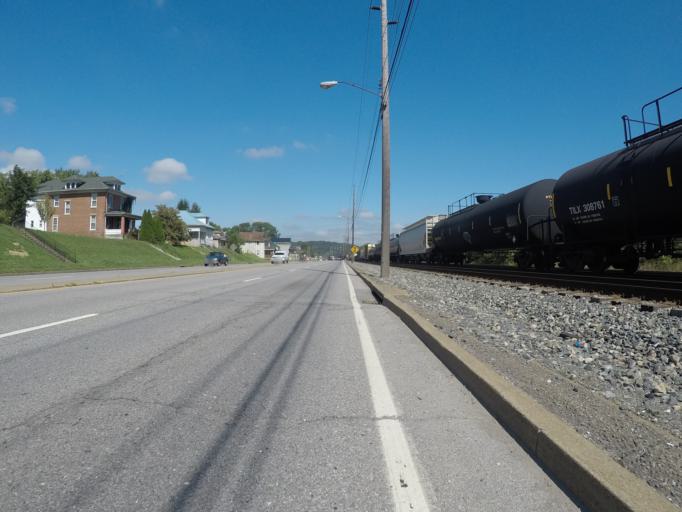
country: US
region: Ohio
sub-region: Lawrence County
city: South Point
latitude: 38.4405
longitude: -82.6092
